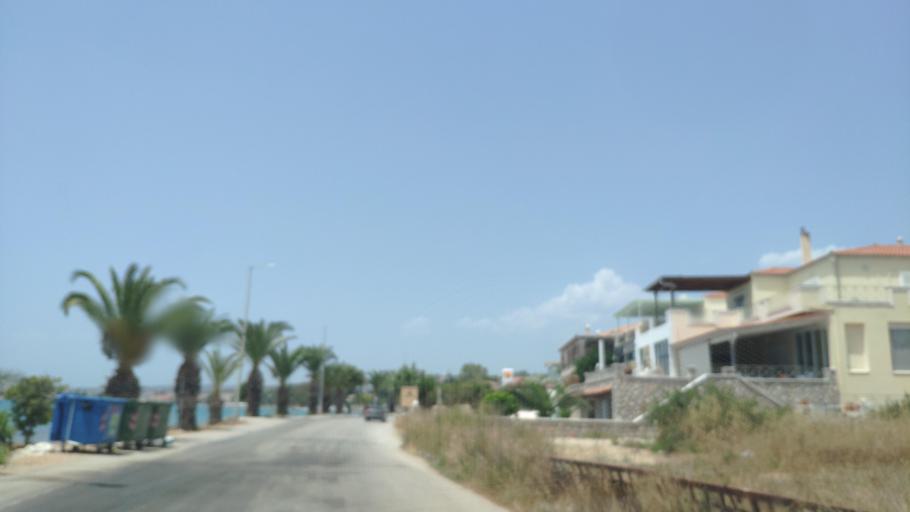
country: GR
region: Peloponnese
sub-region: Nomos Argolidos
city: Porto Cheli
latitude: 37.3207
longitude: 23.1573
